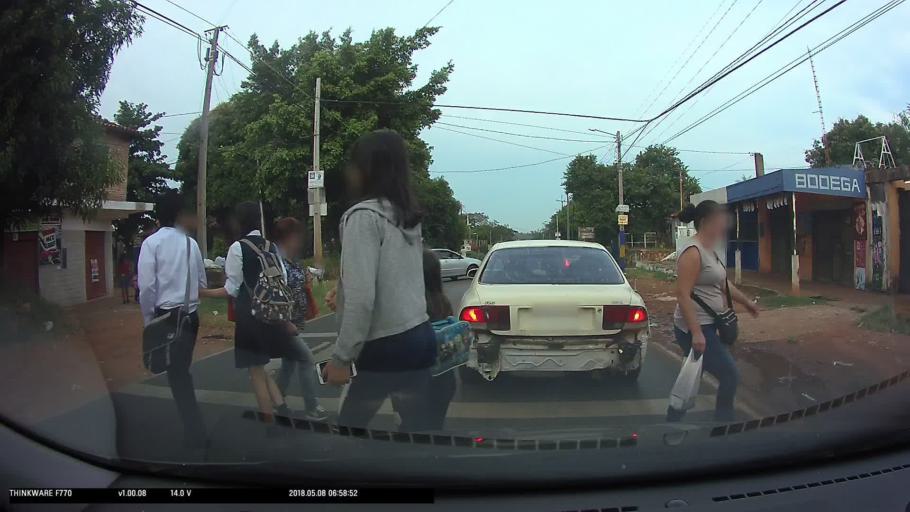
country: PY
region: Central
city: Limpio
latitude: -25.2459
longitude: -57.4826
